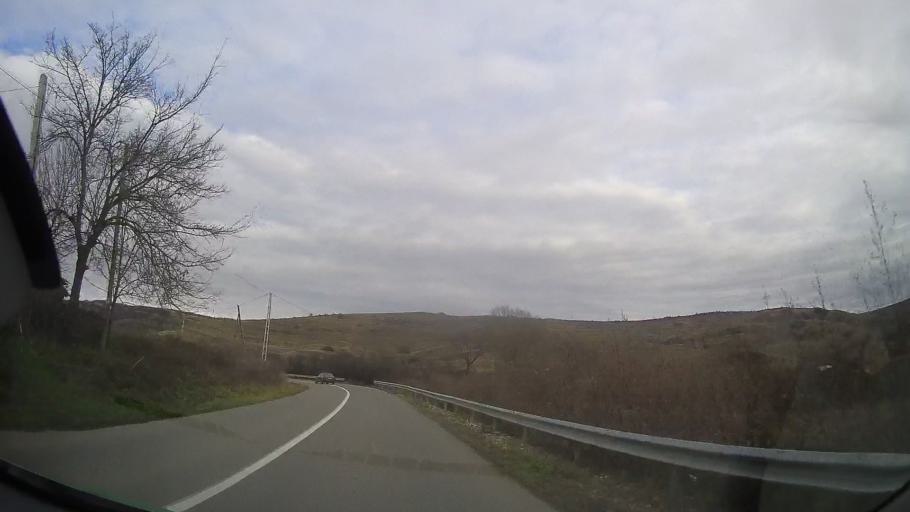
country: RO
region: Bistrita-Nasaud
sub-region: Comuna Milas
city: Milas
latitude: 46.8357
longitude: 24.4482
